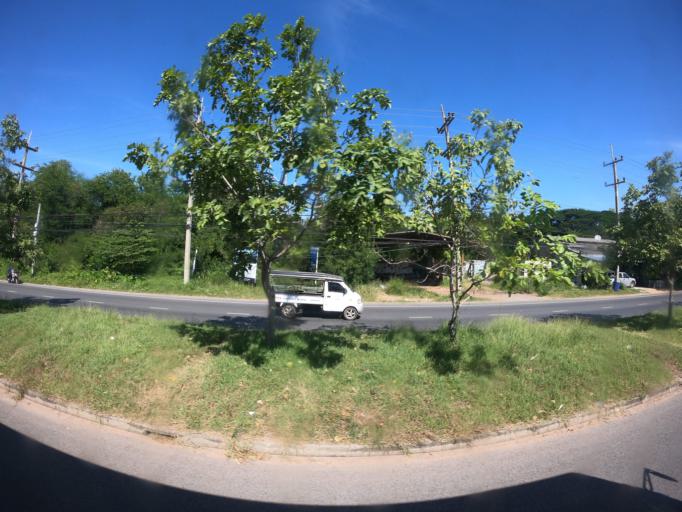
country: TH
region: Nakhon Ratchasima
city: Nakhon Ratchasima
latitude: 14.9986
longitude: 102.1155
